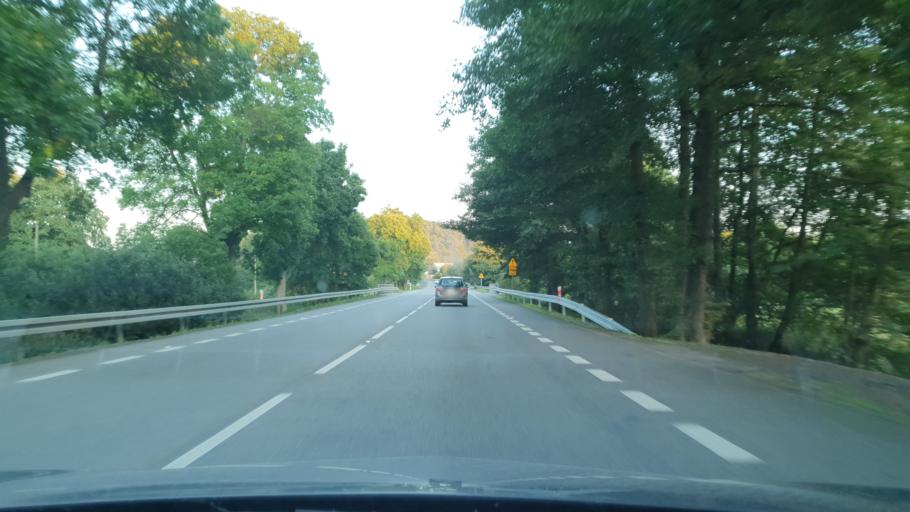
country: PL
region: Pomeranian Voivodeship
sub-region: Powiat leborski
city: Nowa Wies Leborska
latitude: 54.5001
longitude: 17.6287
